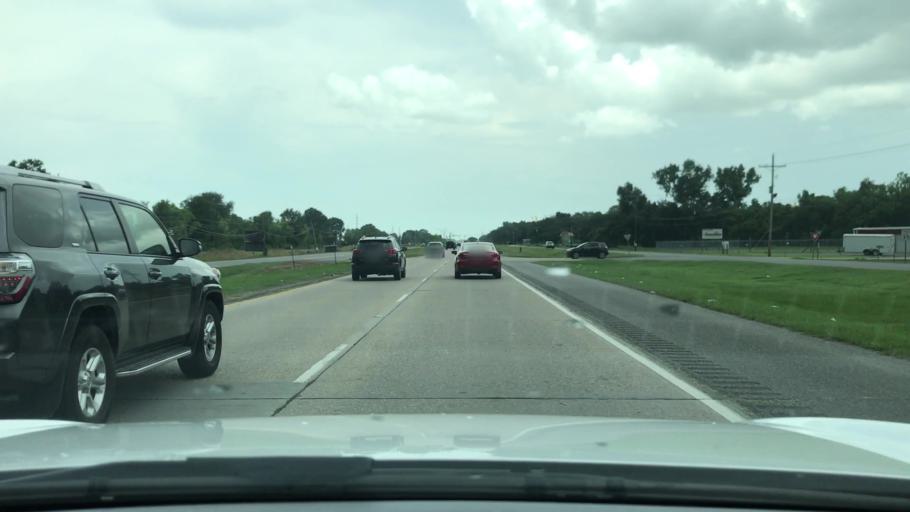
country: US
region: Louisiana
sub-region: Iberville Parish
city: Plaquemine
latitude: 30.3090
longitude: -91.2465
